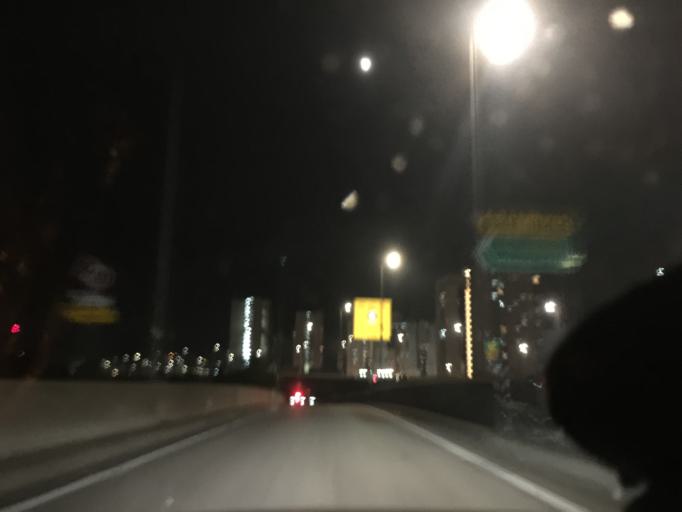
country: MY
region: Kuala Lumpur
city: Kuala Lumpur
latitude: 3.1647
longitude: 101.7328
